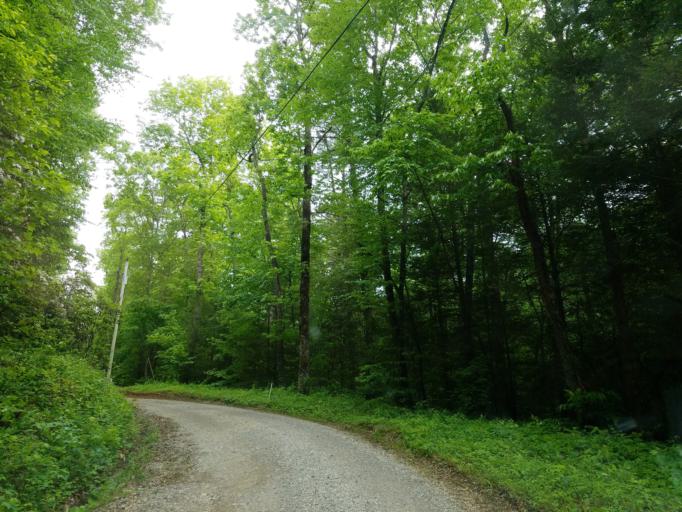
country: US
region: Georgia
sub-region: Union County
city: Blairsville
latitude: 34.7325
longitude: -83.9698
